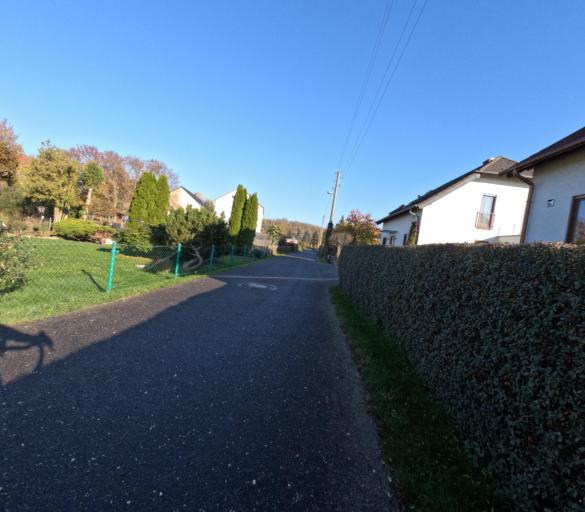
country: DE
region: Saxony
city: Otterwisch
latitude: 51.2483
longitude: 12.6412
